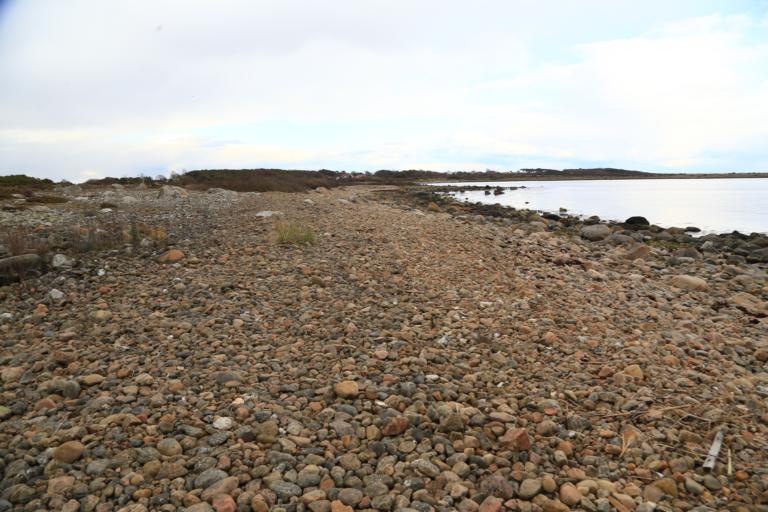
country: SE
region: Halland
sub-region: Varbergs Kommun
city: Traslovslage
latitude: 57.0481
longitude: 12.2769
